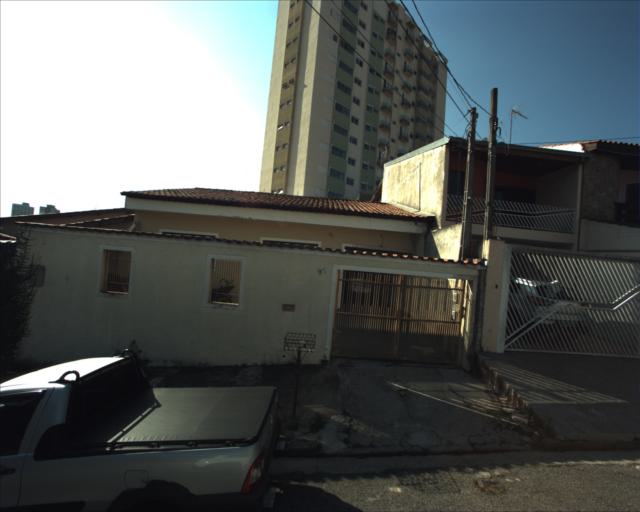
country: BR
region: Sao Paulo
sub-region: Sorocaba
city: Sorocaba
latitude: -23.4951
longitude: -47.4261
